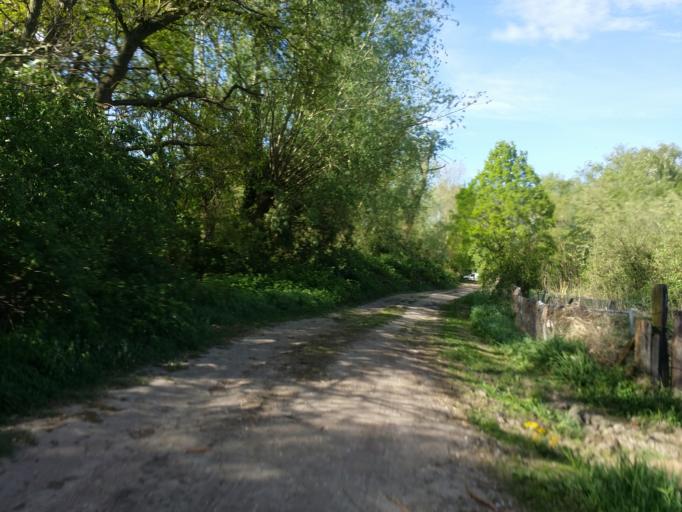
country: DE
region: Lower Saxony
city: Lemwerder
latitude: 53.1571
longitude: 8.6658
